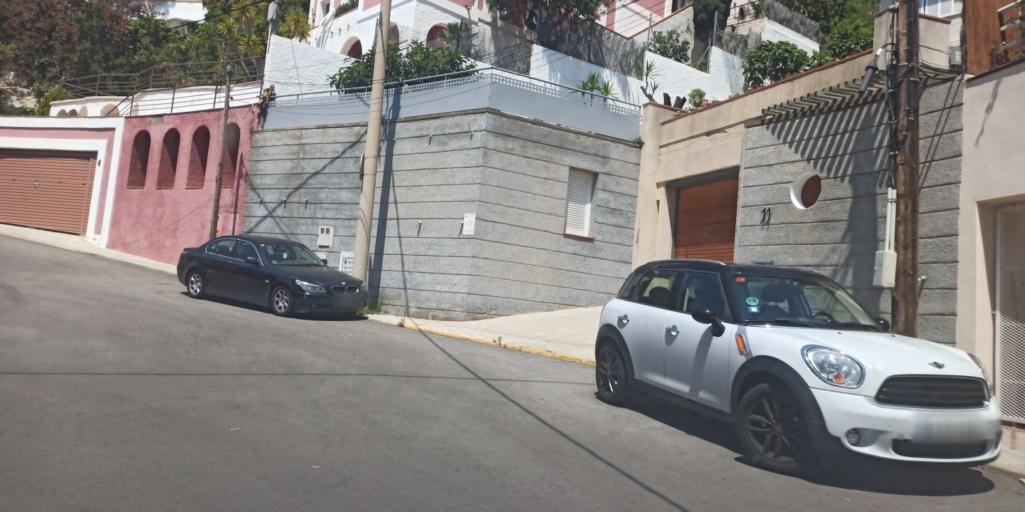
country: ES
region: Catalonia
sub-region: Provincia de Barcelona
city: Sitges
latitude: 41.2420
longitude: 1.8255
